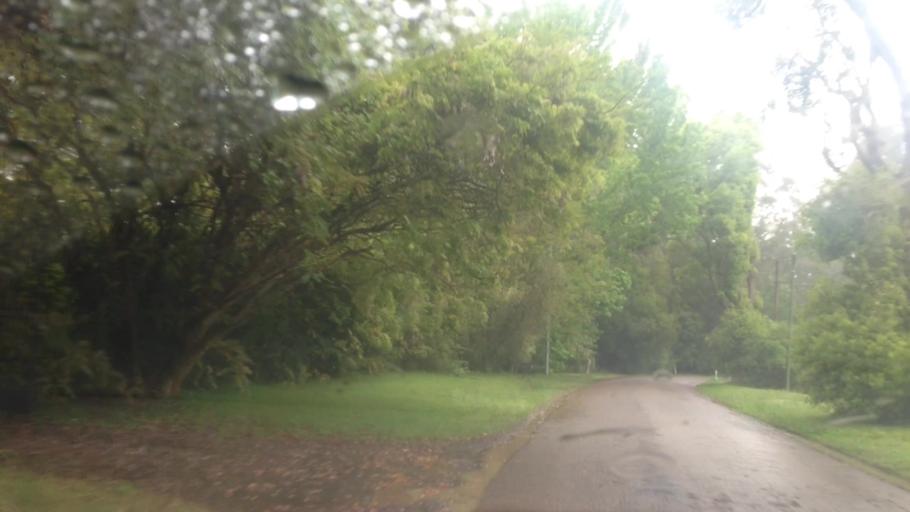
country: AU
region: New South Wales
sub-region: Wyong Shire
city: Little Jilliby
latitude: -33.1877
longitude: 151.3619
